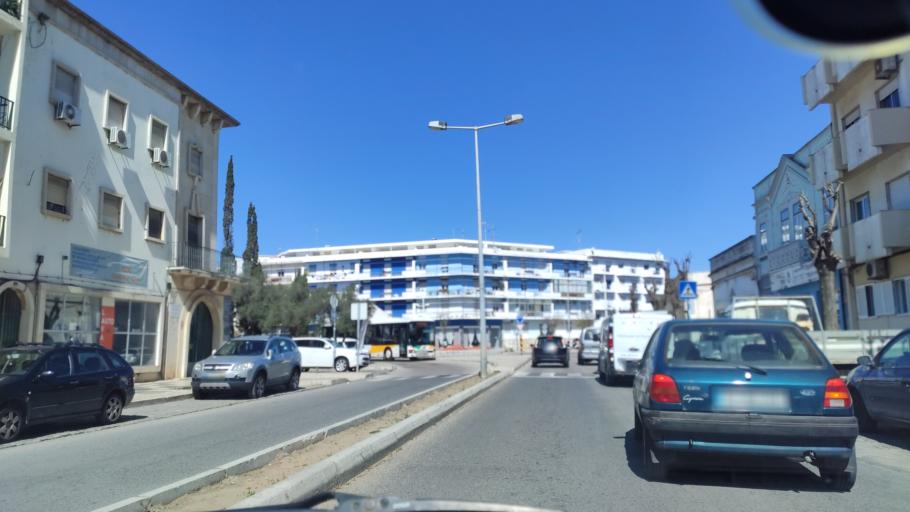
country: PT
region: Faro
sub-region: Olhao
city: Olhao
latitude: 37.0343
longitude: -7.8367
